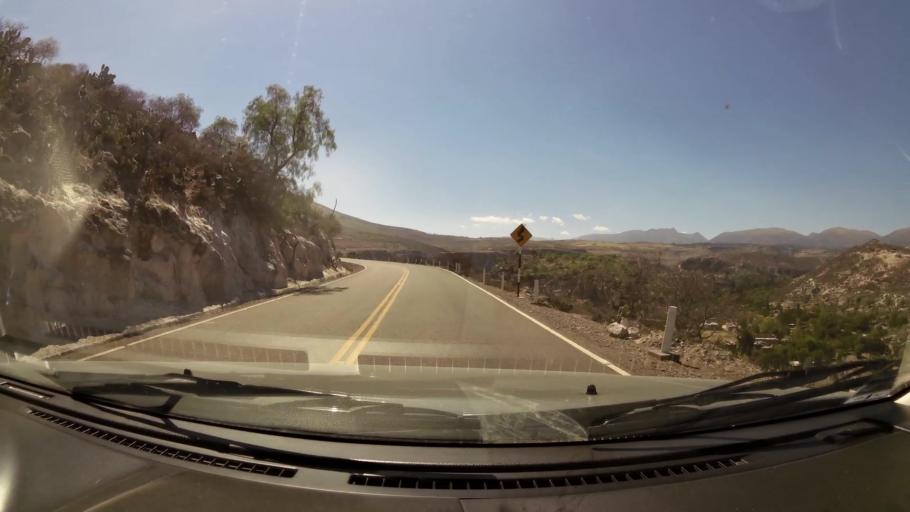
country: PE
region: Ayacucho
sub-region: Provincia de Huamanga
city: Pacaycasa
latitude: -13.0689
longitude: -74.2214
